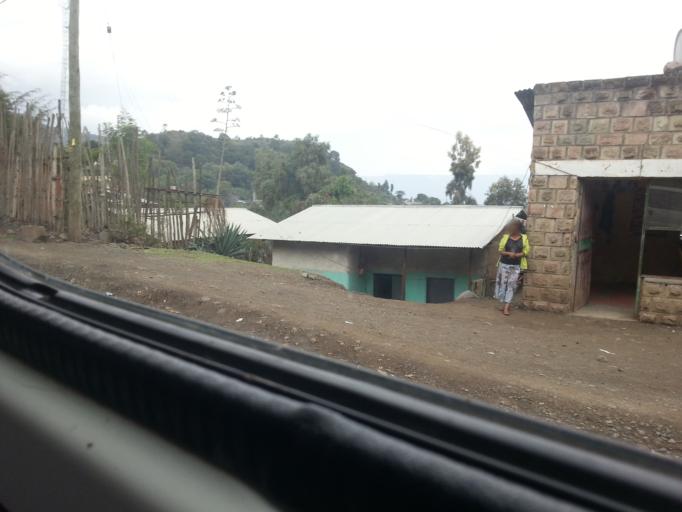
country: ET
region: Amhara
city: Lalibela
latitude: 12.0379
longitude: 39.0450
